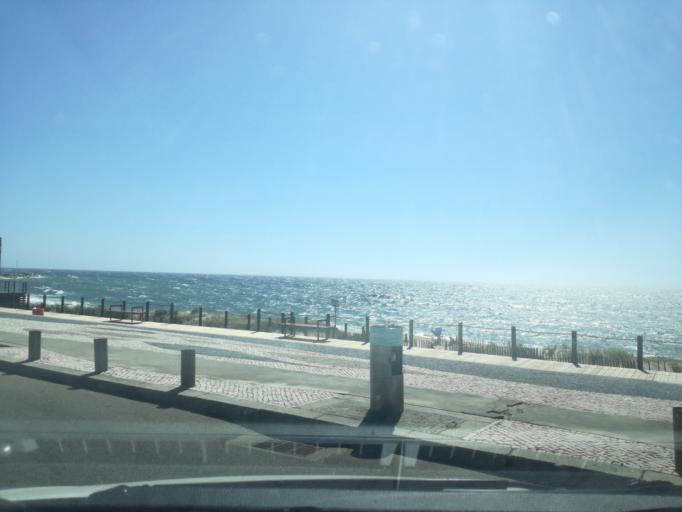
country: PT
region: Porto
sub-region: Matosinhos
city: Lavra
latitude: 41.2687
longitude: -8.7263
